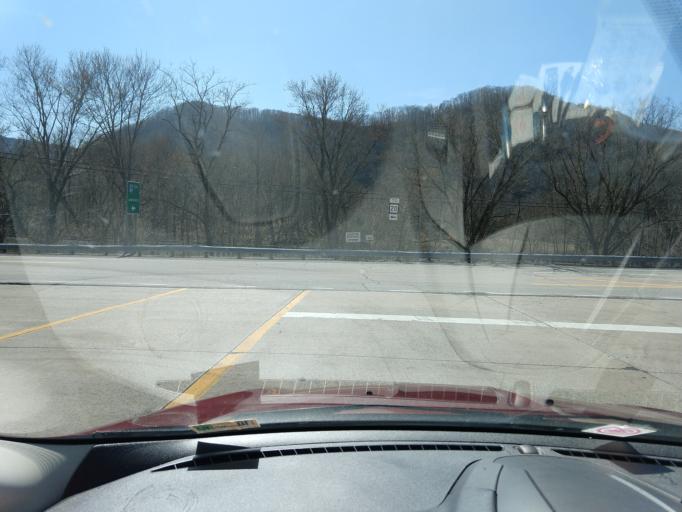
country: US
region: West Virginia
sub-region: Summers County
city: Hinton
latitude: 37.7797
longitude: -80.8930
